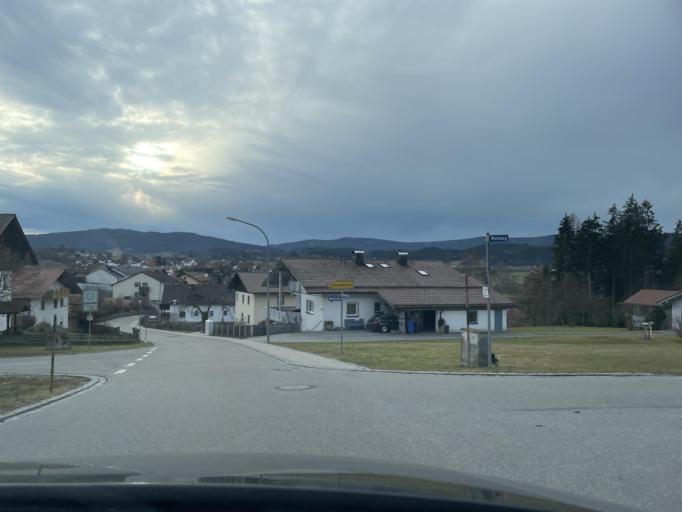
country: DE
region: Bavaria
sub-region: Lower Bavaria
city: Ruhmannsfelden
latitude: 48.9905
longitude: 12.9969
